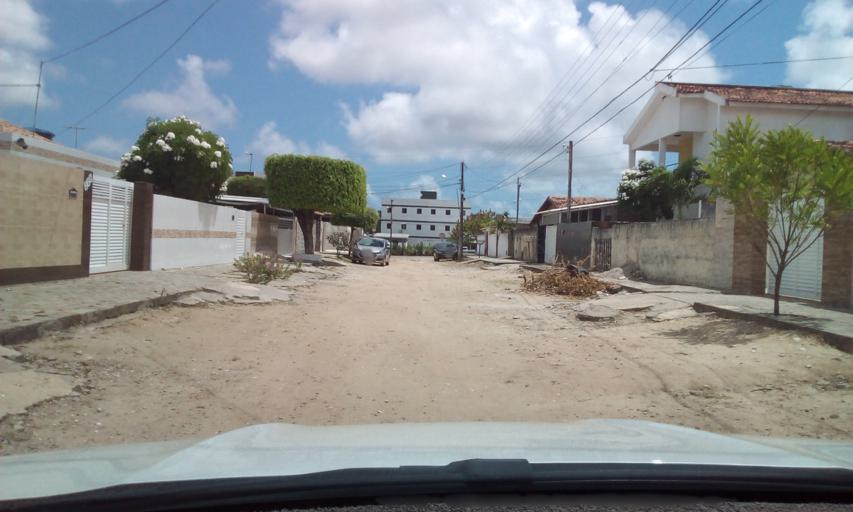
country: BR
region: Paraiba
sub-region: Joao Pessoa
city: Joao Pessoa
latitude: -7.1785
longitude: -34.8655
